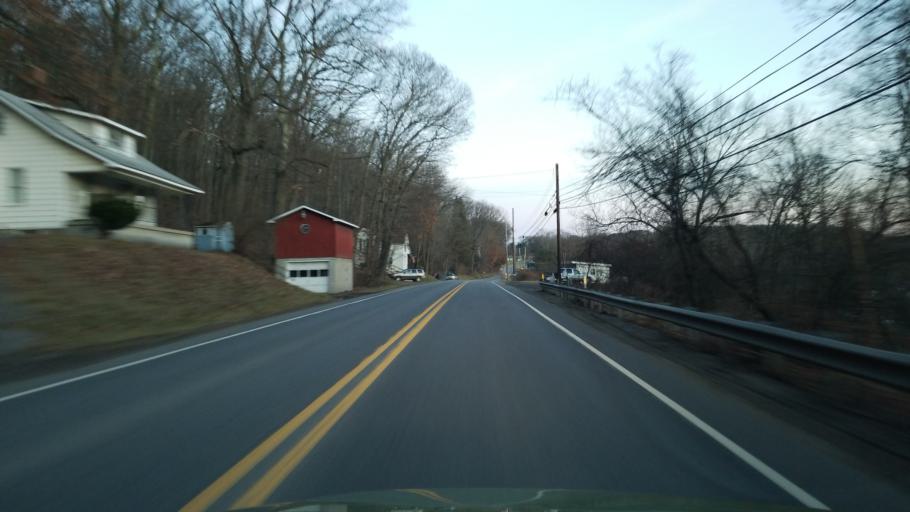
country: US
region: Pennsylvania
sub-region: Jefferson County
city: Albion
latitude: 40.9528
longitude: -78.9461
